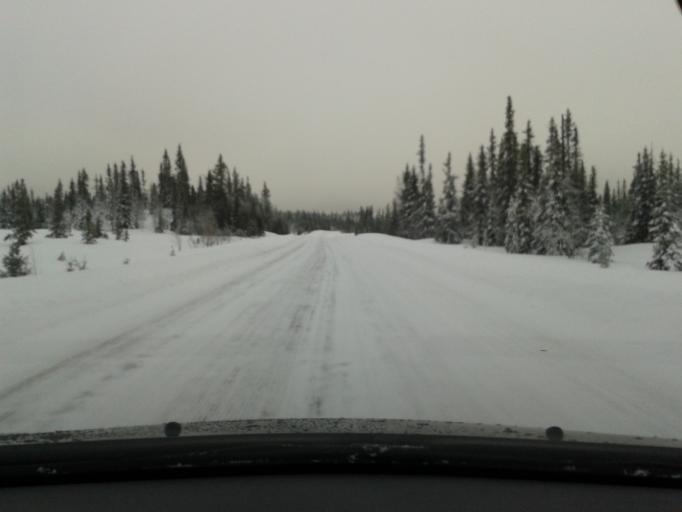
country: SE
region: Vaesterbotten
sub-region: Vilhelmina Kommun
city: Sjoberg
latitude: 65.0819
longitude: 15.8779
